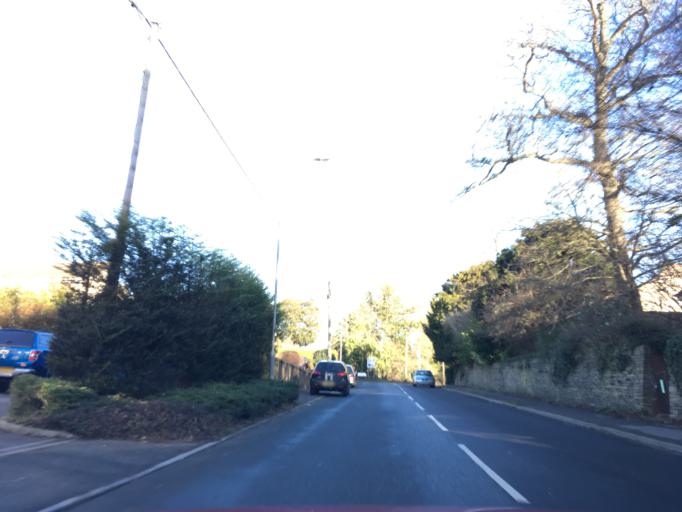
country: GB
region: England
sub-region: Wiltshire
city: Chippenham
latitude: 51.4696
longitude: -2.1124
